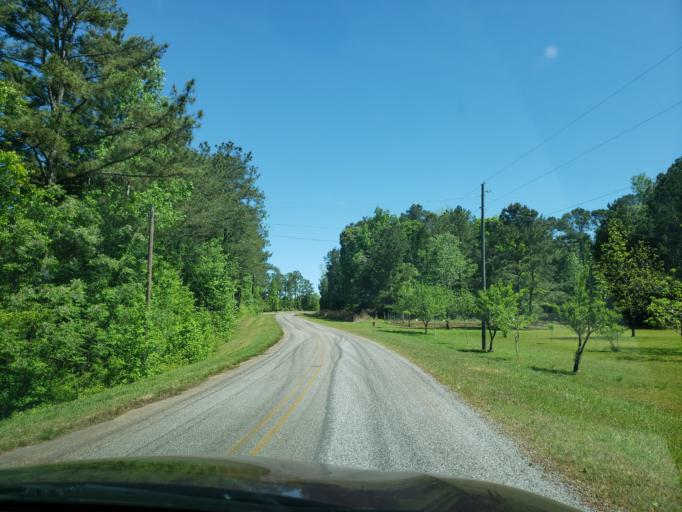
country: US
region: Alabama
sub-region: Elmore County
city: Eclectic
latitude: 32.6991
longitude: -85.8883
